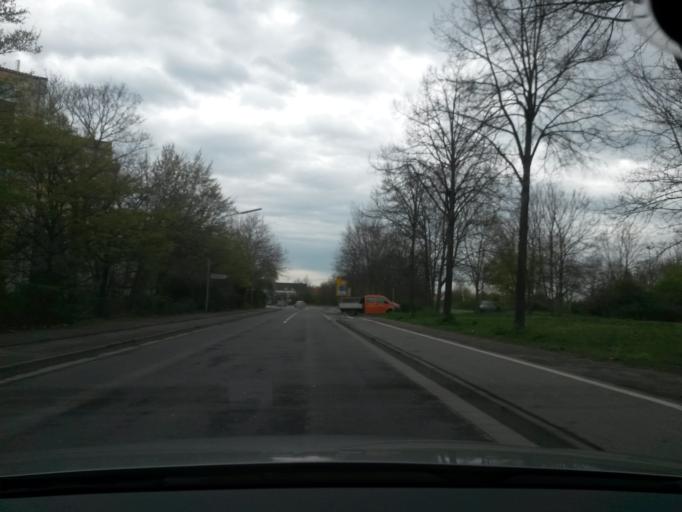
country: DE
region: Rheinland-Pfalz
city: Worms
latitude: 49.6491
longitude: 8.3430
